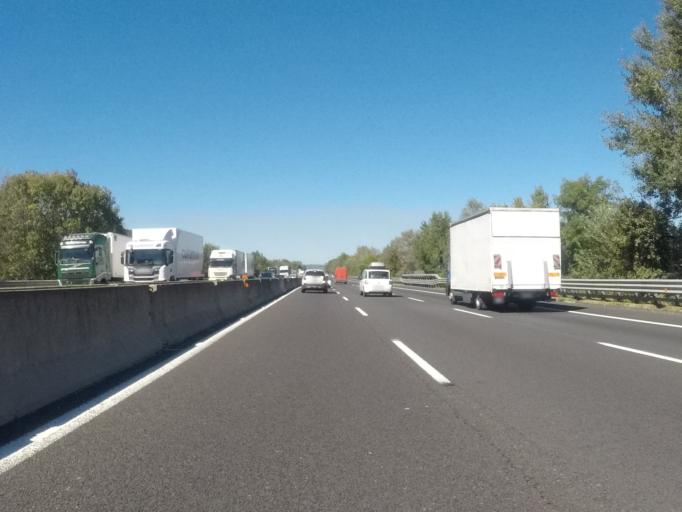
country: IT
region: Umbria
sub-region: Provincia di Terni
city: Otricoli
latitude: 42.4043
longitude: 12.4538
